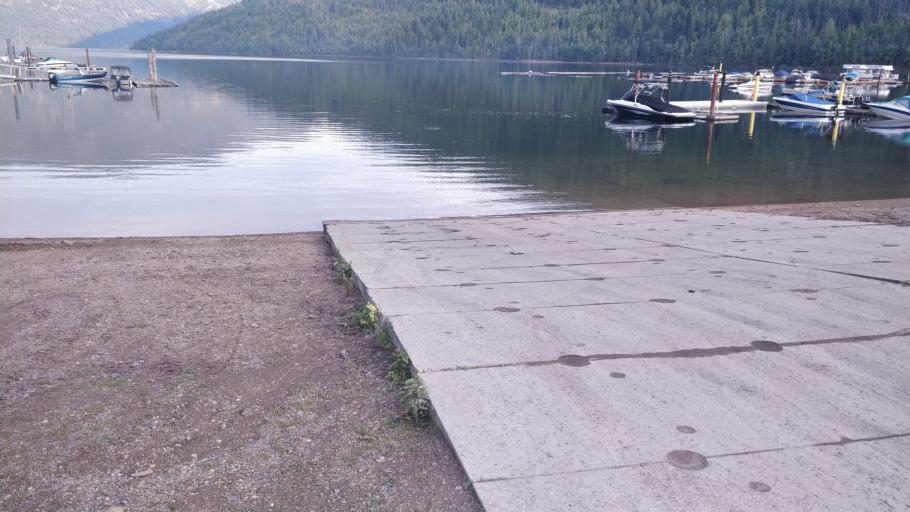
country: CA
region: British Columbia
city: Chase
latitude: 51.0789
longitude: -119.7861
